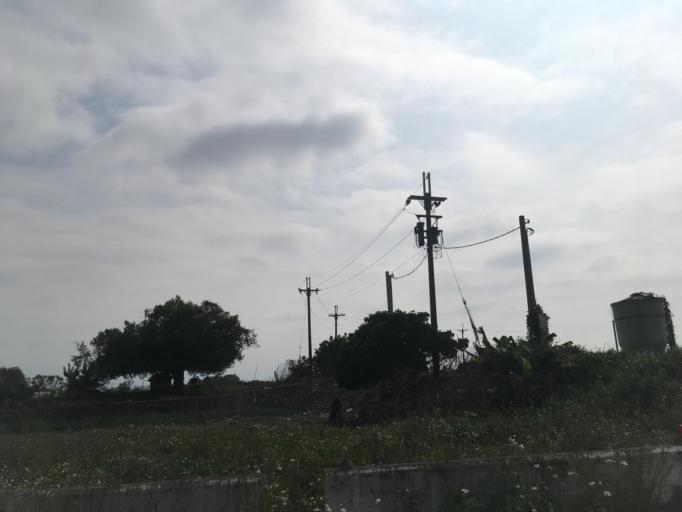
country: TW
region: Taiwan
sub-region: Yunlin
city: Douliu
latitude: 23.6965
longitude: 120.4526
